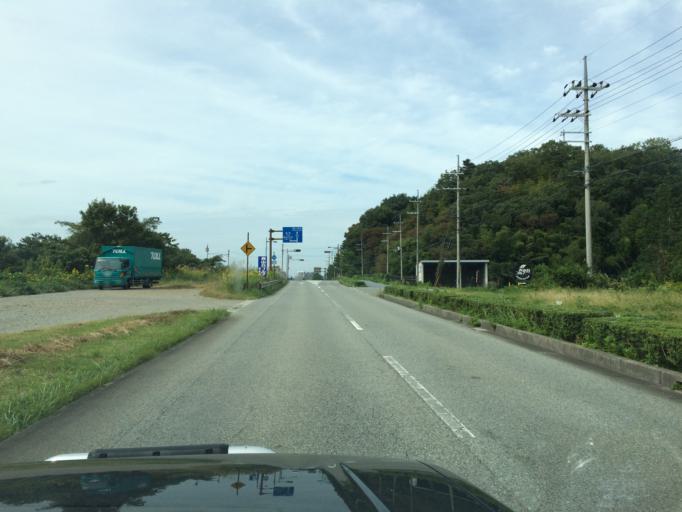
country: JP
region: Hyogo
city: Sasayama
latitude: 35.0730
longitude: 135.2502
